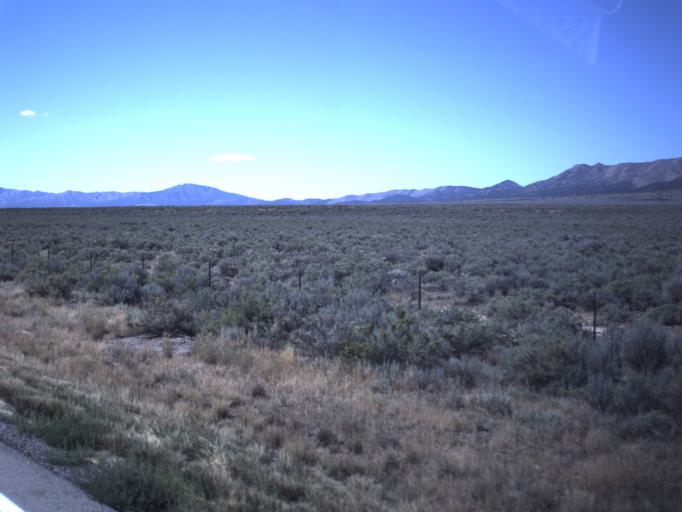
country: US
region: Utah
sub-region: Tooele County
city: Tooele
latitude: 40.2335
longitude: -112.4028
